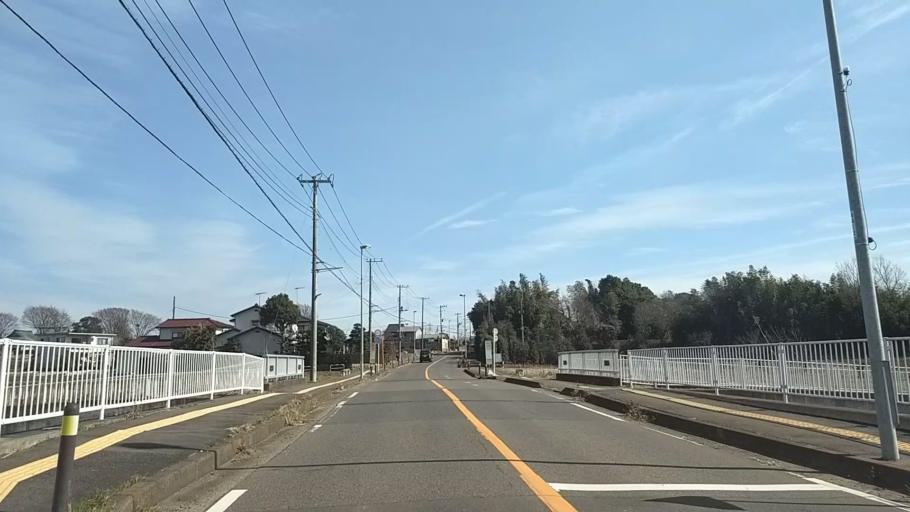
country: JP
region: Kanagawa
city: Chigasaki
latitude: 35.3871
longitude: 139.4091
